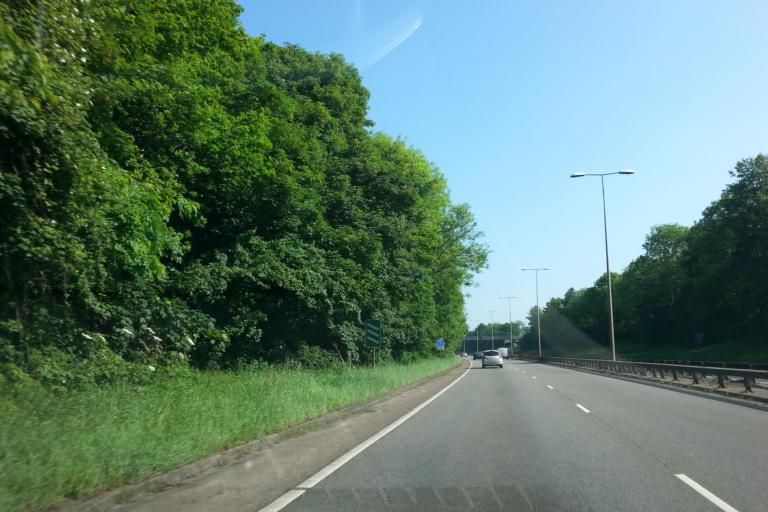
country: GB
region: England
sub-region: Peterborough
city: Marholm
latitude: 52.5815
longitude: -0.2821
